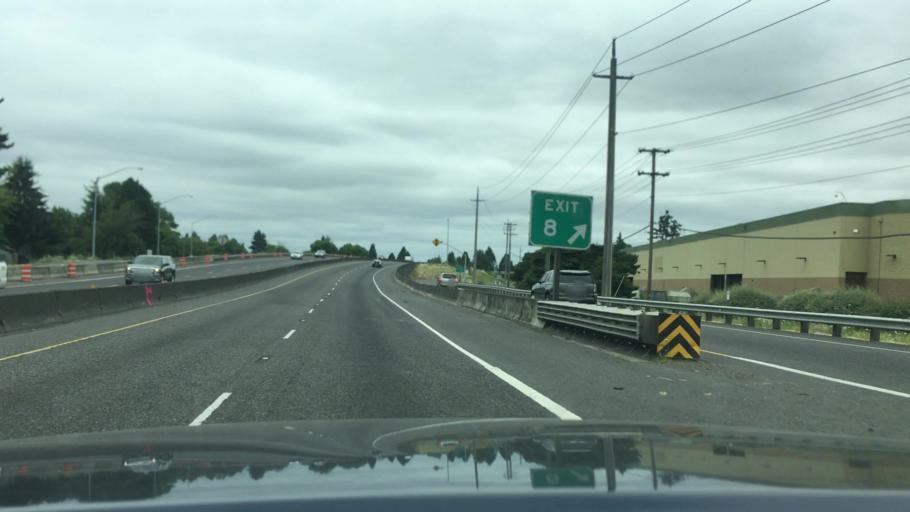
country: US
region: Oregon
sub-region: Lane County
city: Eugene
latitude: 44.0975
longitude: -123.1245
